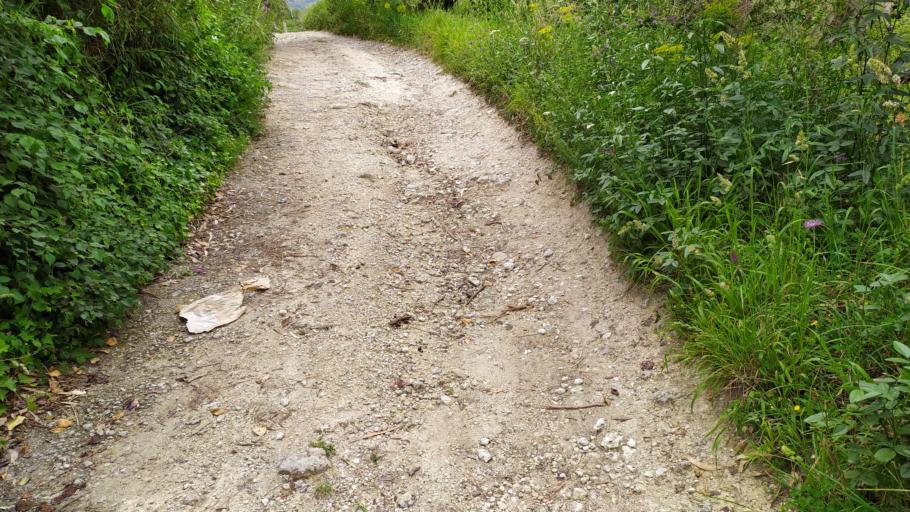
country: IT
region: Sicily
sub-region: Messina
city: Gualtieri Sicamino
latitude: 38.1549
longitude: 15.3007
